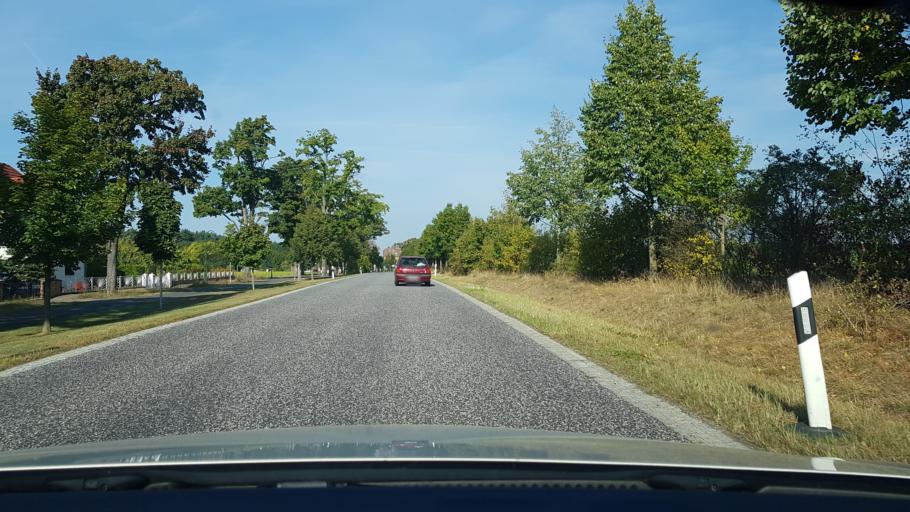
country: DE
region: Brandenburg
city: Mixdorf
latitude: 52.1618
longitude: 14.3838
